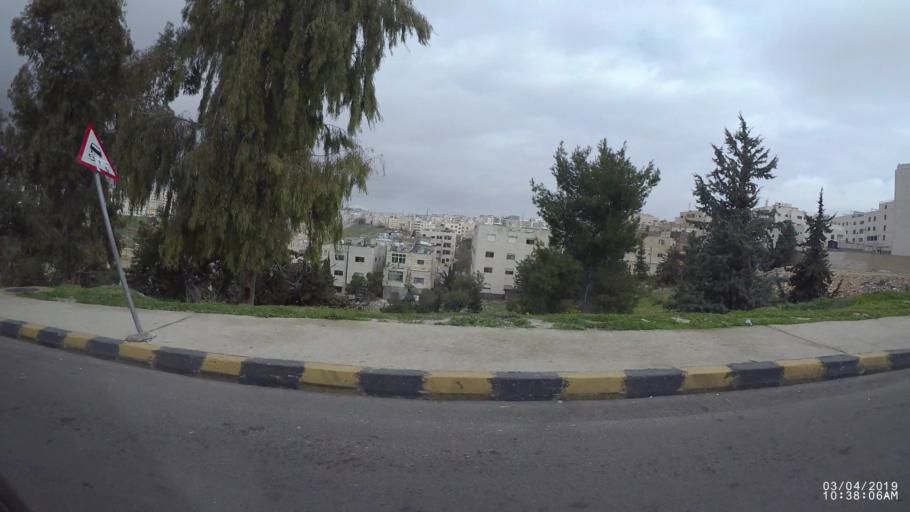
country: JO
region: Amman
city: Wadi as Sir
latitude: 31.9548
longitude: 35.8319
